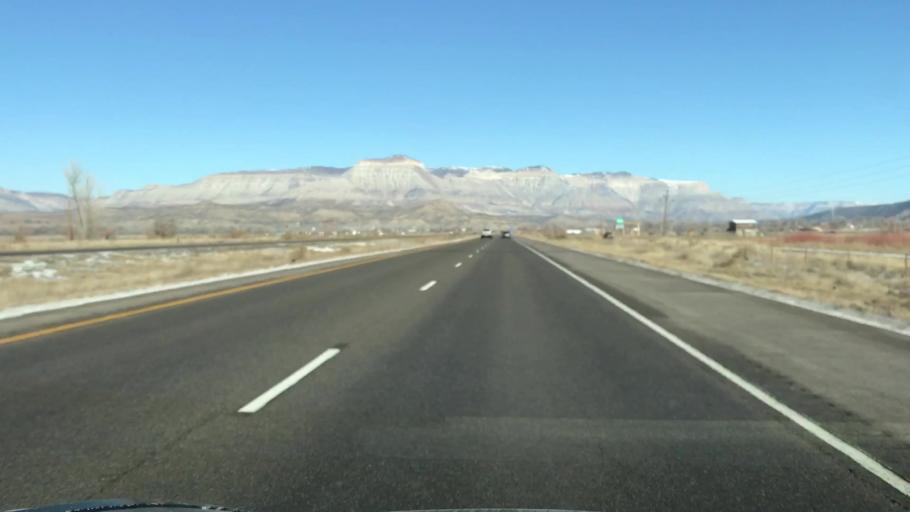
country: US
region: Colorado
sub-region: Mesa County
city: Palisade
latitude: 39.2963
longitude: -108.2212
